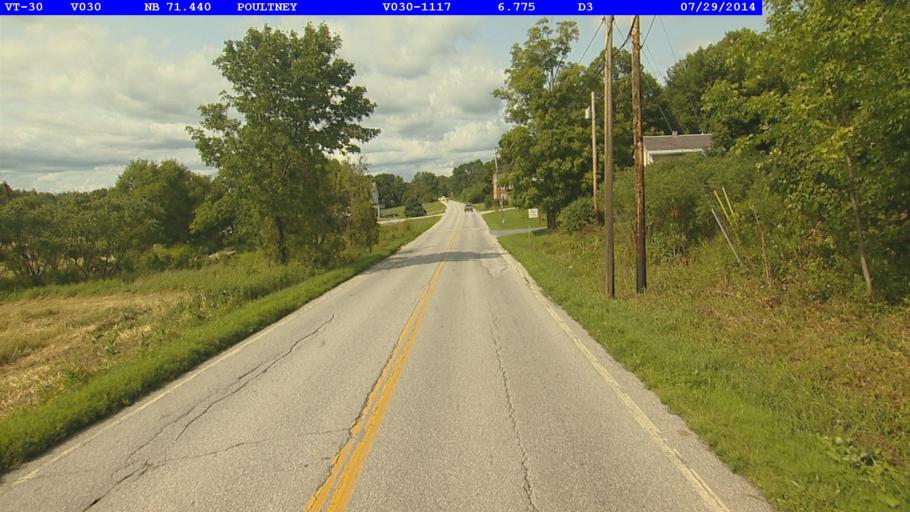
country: US
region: Vermont
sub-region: Rutland County
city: Poultney
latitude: 43.5485
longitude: -73.2269
